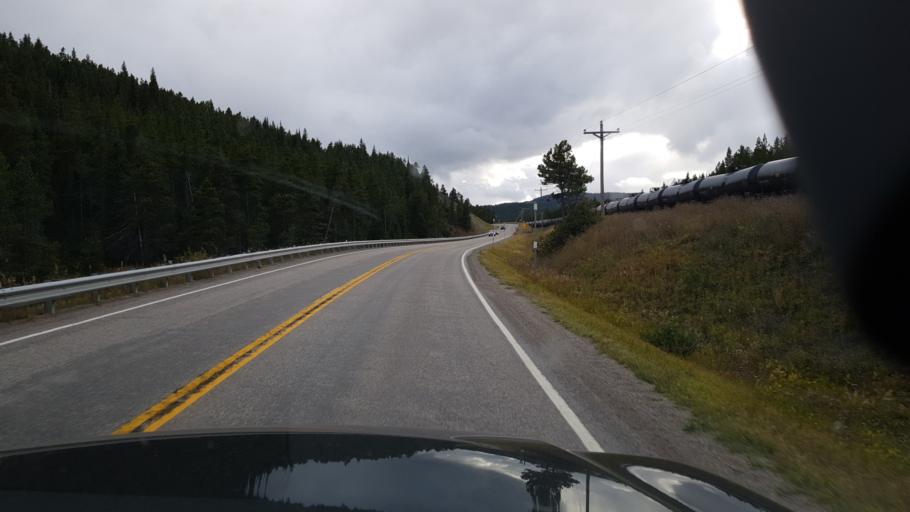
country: US
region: Montana
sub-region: Glacier County
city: South Browning
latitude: 48.3252
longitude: -113.3443
